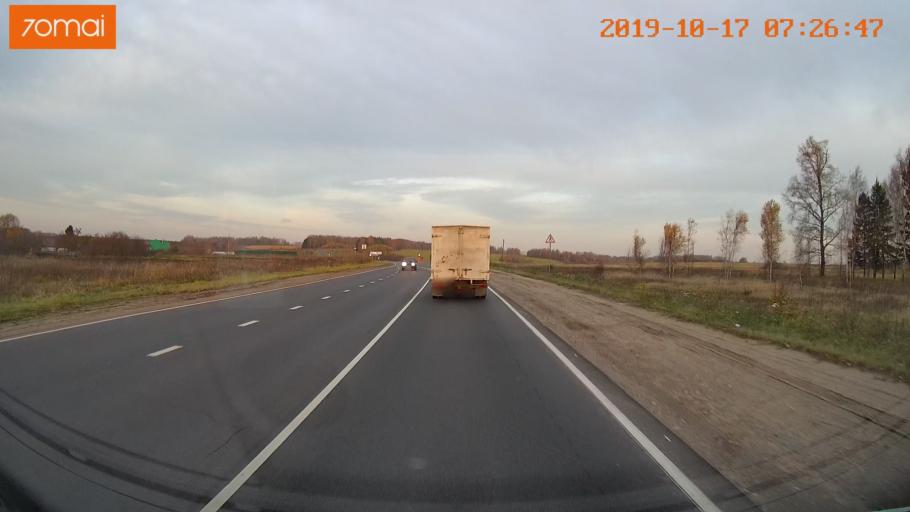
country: RU
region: Ivanovo
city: Gavrilov Posad
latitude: 56.3596
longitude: 40.0890
